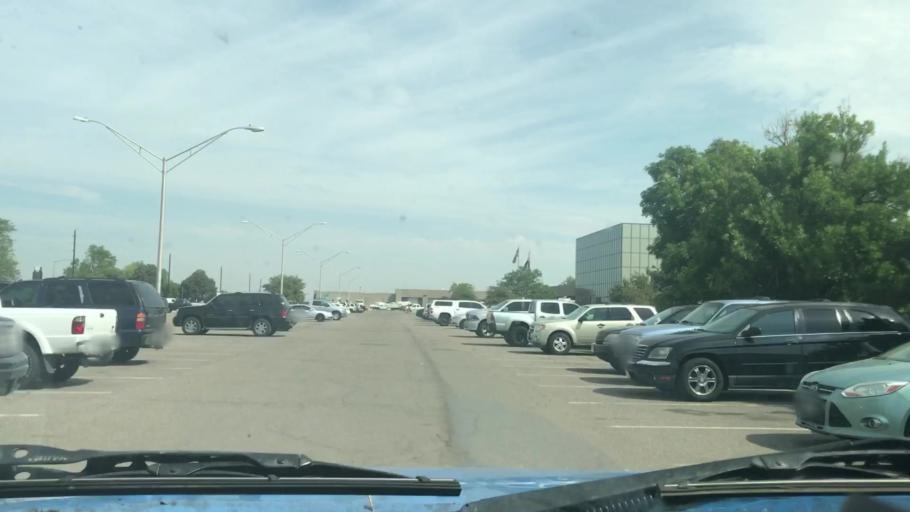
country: US
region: Colorado
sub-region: Adams County
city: Commerce City
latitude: 39.7947
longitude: -104.9007
